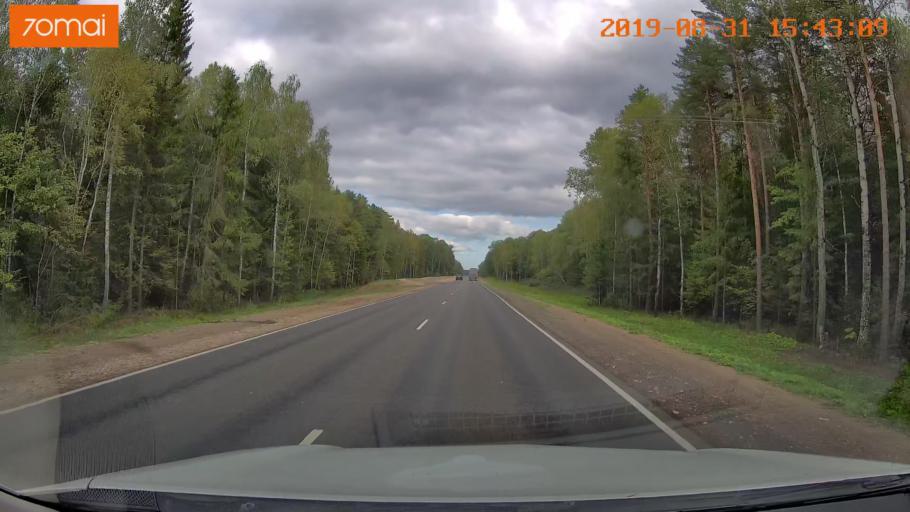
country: RU
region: Kaluga
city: Mosal'sk
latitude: 54.6512
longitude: 34.9041
